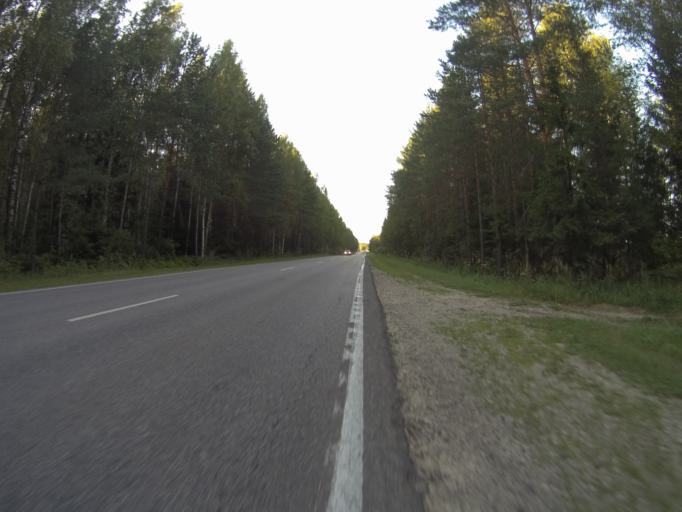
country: RU
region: Vladimir
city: Anopino
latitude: 55.6786
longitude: 40.7404
